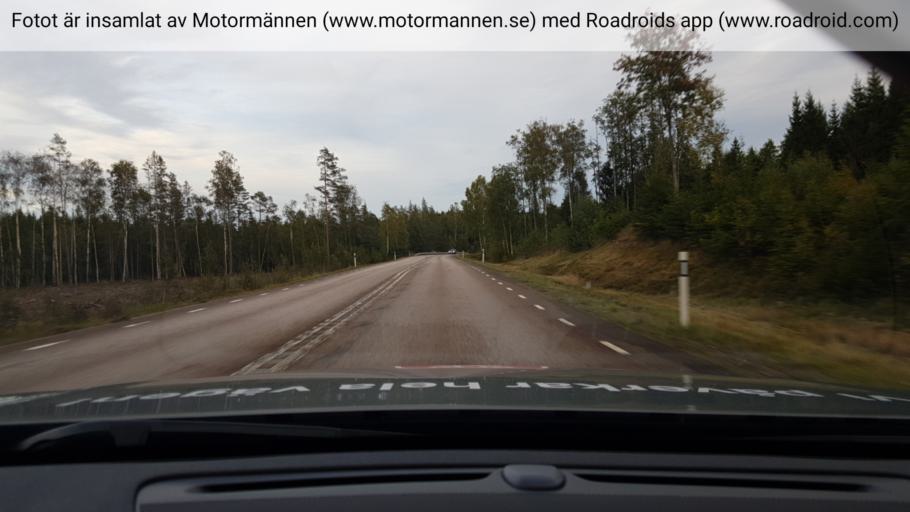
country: SE
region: Vaestra Goetaland
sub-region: Amals Kommun
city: Amal
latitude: 59.0608
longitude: 12.5204
